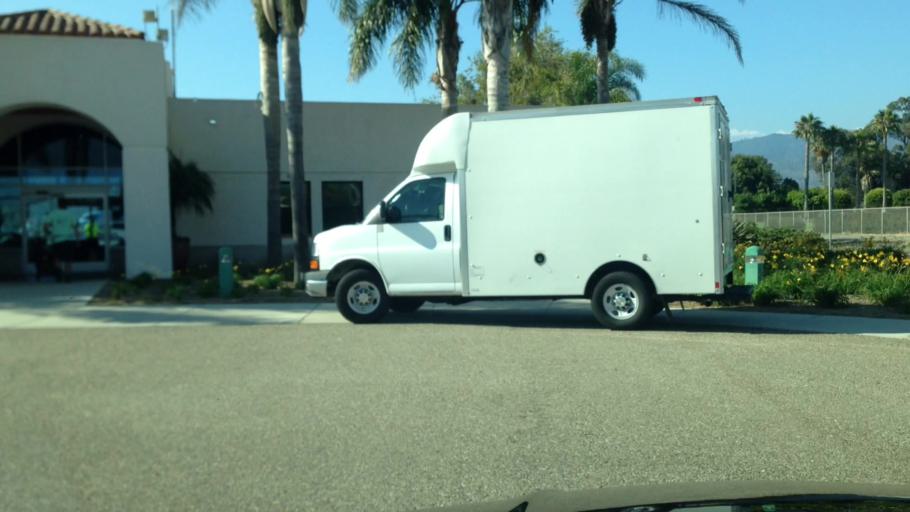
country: US
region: California
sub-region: Santa Barbara County
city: Goleta
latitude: 34.4222
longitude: -119.8354
